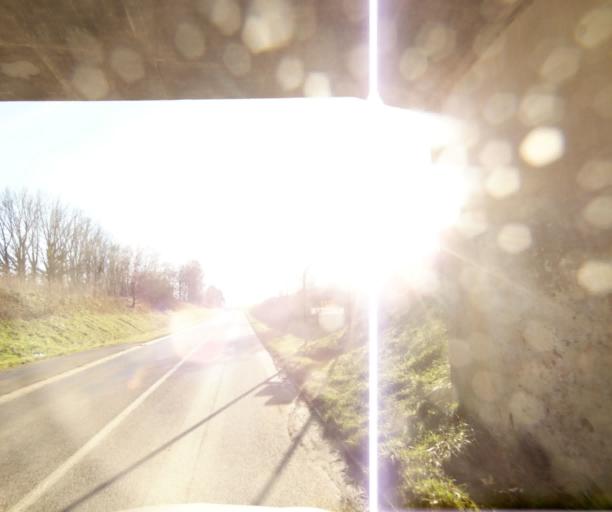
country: FR
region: Nord-Pas-de-Calais
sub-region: Departement du Nord
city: Saultain
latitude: 50.3315
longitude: 3.5752
